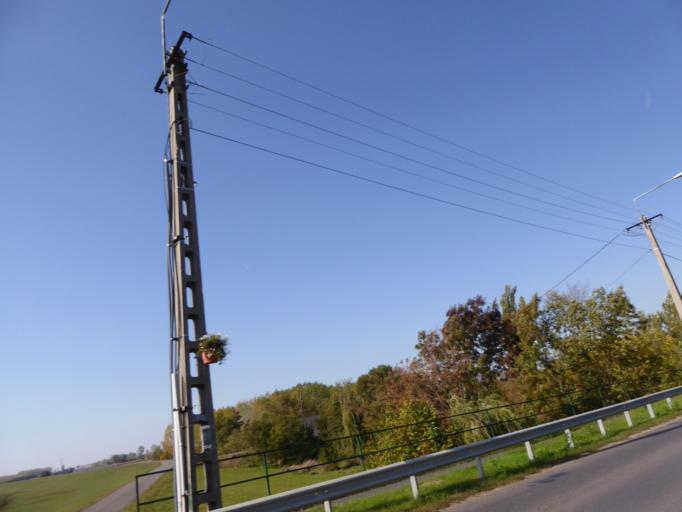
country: HU
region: Hajdu-Bihar
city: Berettyoujfalu
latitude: 47.2064
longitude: 21.5392
